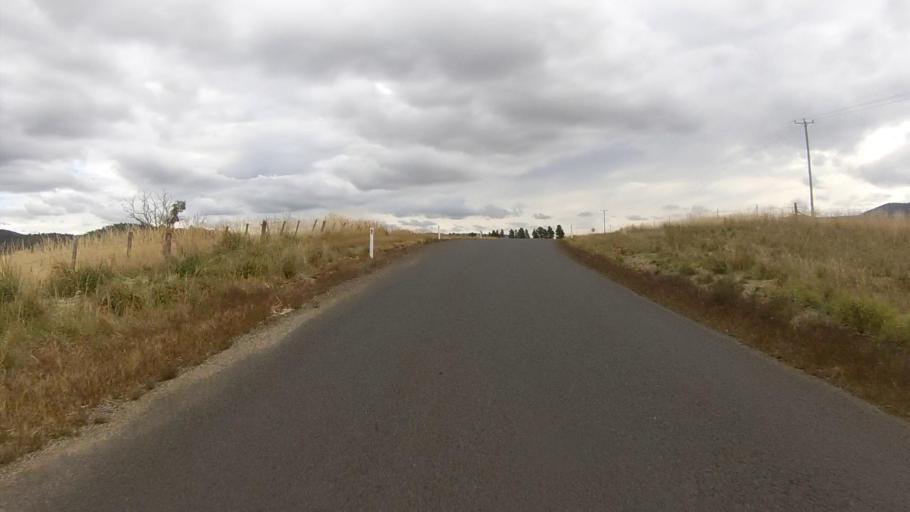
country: AU
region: Tasmania
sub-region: Break O'Day
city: St Helens
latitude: -41.8249
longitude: 147.8423
